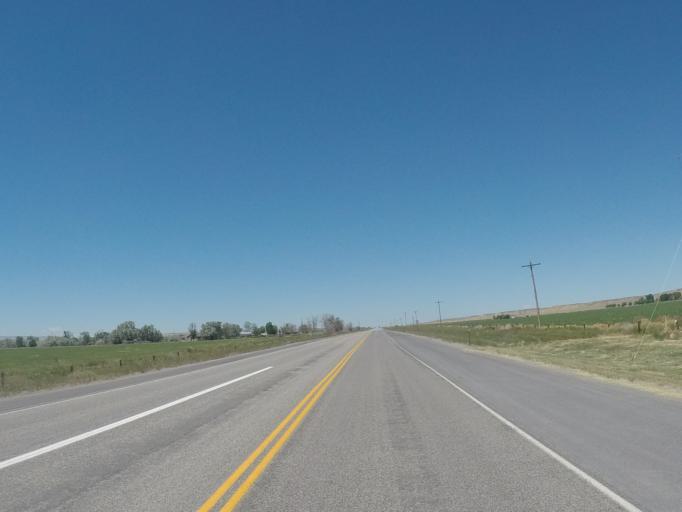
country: US
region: Wyoming
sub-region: Big Horn County
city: Greybull
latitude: 44.5091
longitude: -108.1346
